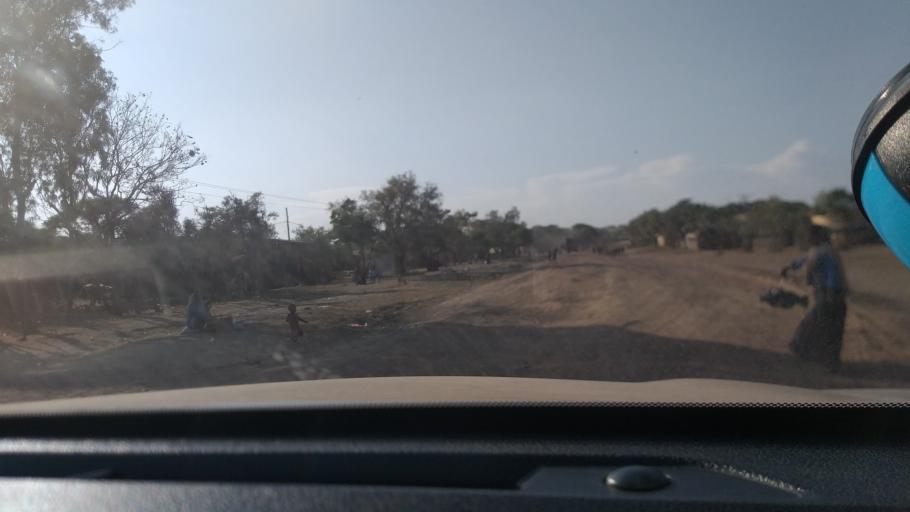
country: ET
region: Oromiya
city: Shashemene
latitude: 7.4899
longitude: 38.7195
